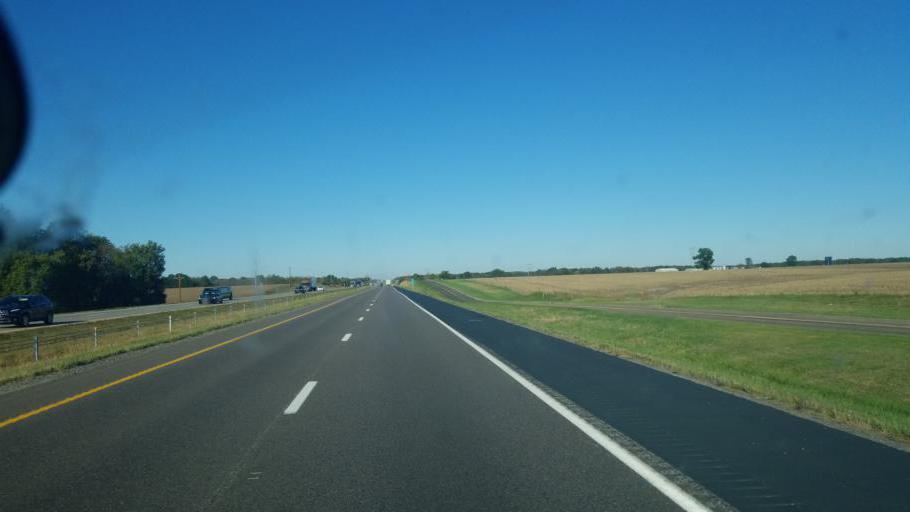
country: US
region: Missouri
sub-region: Callaway County
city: Fulton
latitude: 38.9224
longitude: -91.7634
